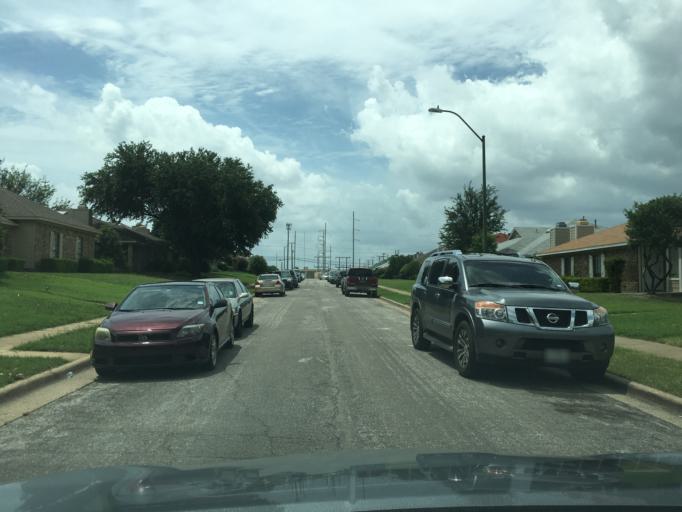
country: US
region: Texas
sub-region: Dallas County
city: Richardson
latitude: 32.9111
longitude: -96.7108
